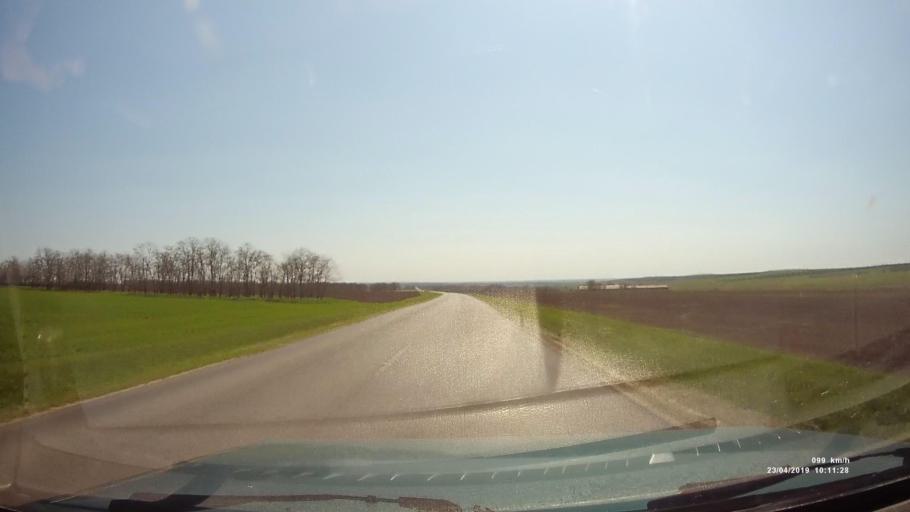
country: RU
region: Rostov
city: Sovetskoye
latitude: 46.6952
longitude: 42.3171
